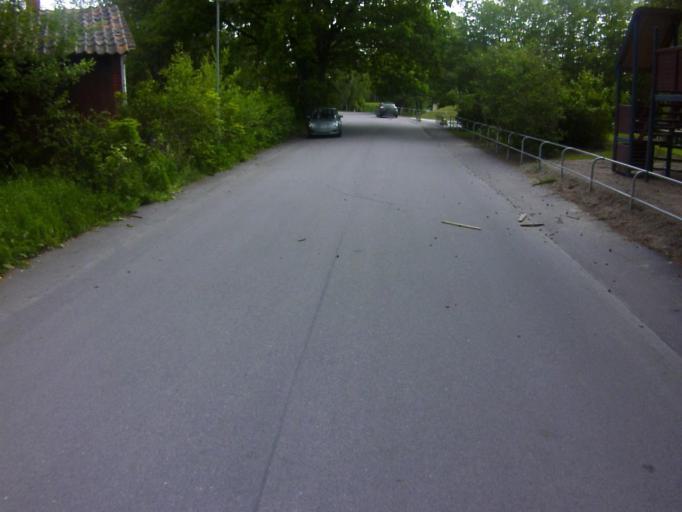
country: SE
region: Soedermanland
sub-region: Eskilstuna Kommun
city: Skogstorp
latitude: 59.3215
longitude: 16.4821
